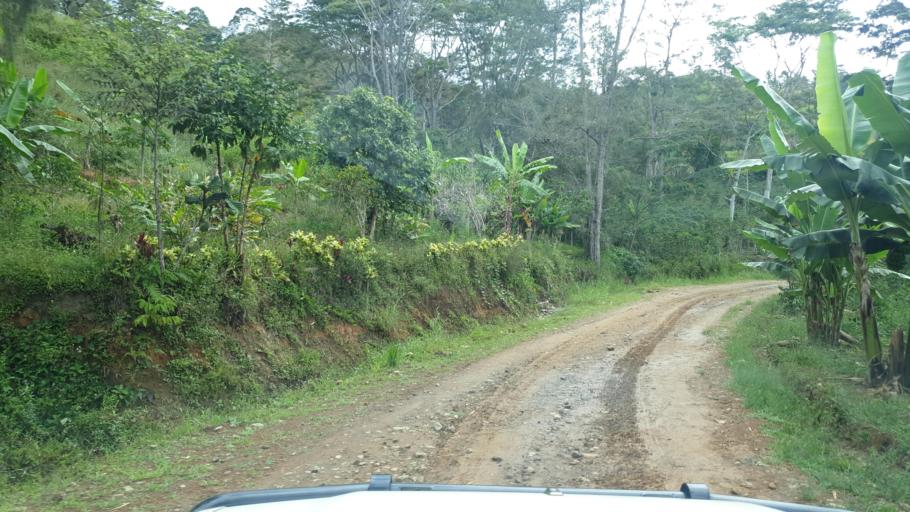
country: PG
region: Eastern Highlands
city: Goroka
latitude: -5.9286
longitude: 145.2639
